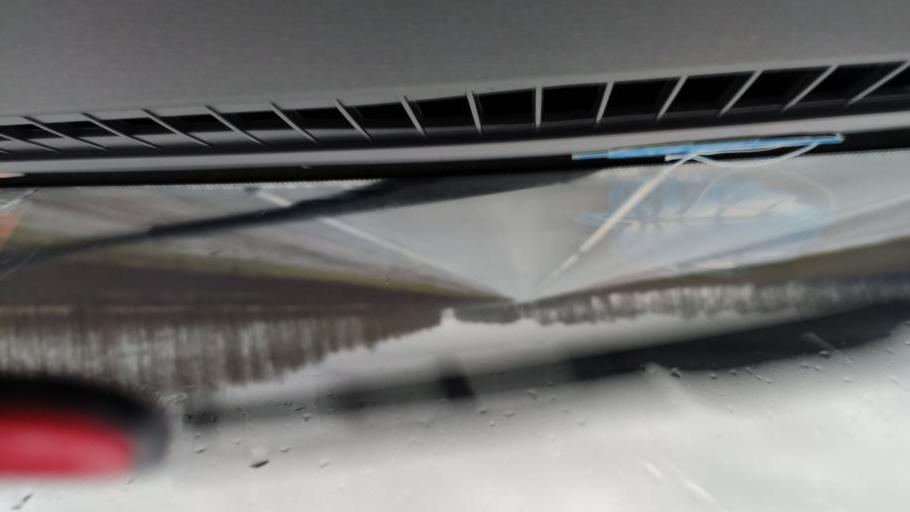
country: RU
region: Tatarstan
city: Mendeleyevsk
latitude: 55.8511
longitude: 52.2103
